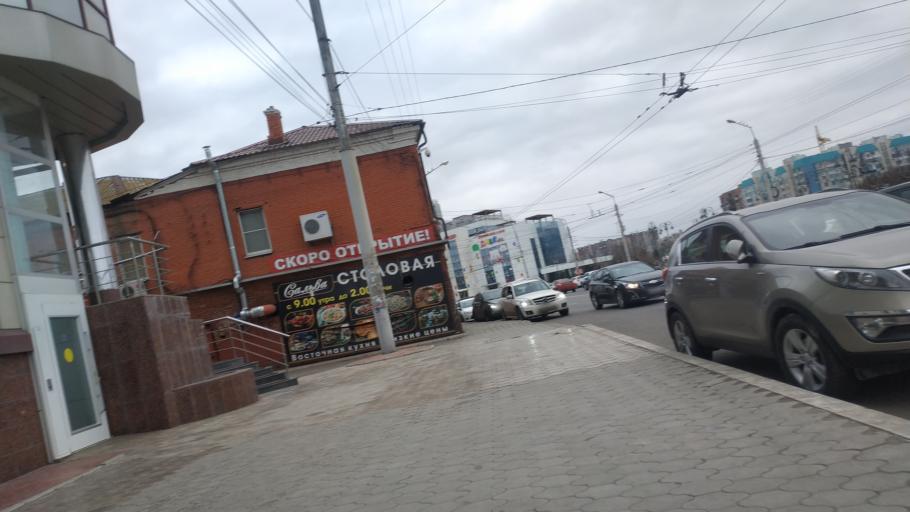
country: RU
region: Astrakhan
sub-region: Gorod Astrakhan'
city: Astrakhan'
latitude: 46.3434
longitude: 48.0214
